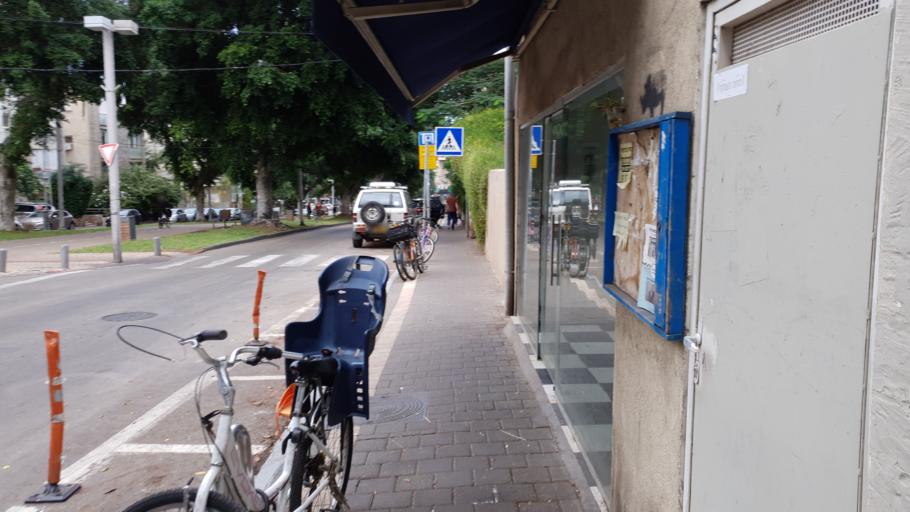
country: IL
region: Tel Aviv
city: Tel Aviv
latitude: 32.0732
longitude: 34.7772
